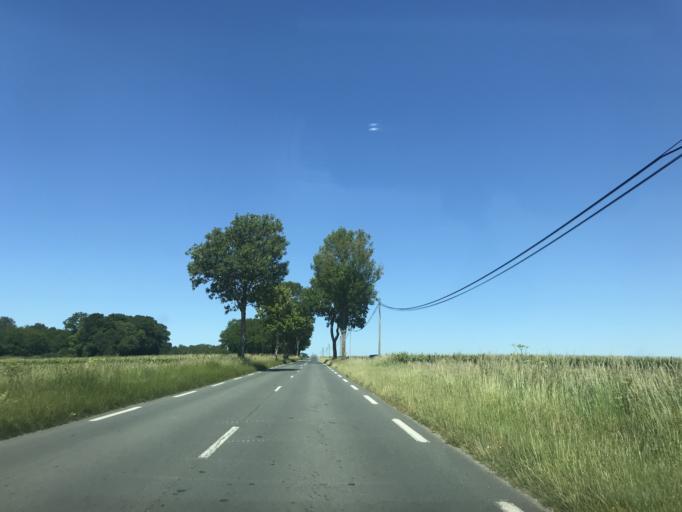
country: FR
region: Poitou-Charentes
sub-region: Departement de la Charente-Maritime
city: Gemozac
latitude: 45.5682
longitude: -0.7359
